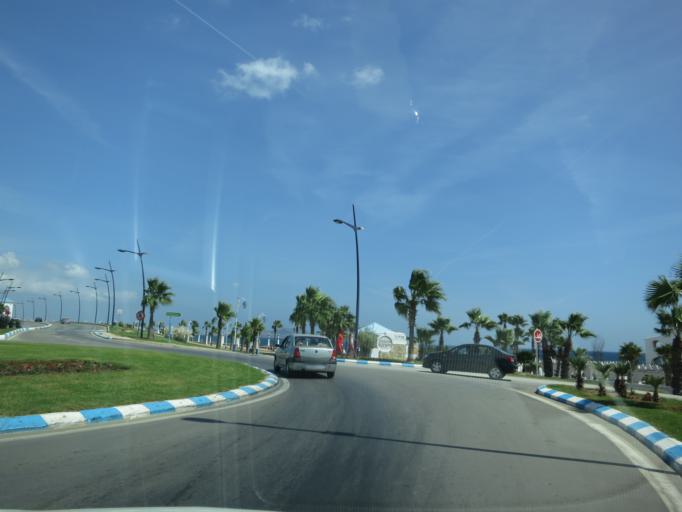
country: ES
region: Ceuta
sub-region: Ceuta
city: Ceuta
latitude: 35.8065
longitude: -5.3528
